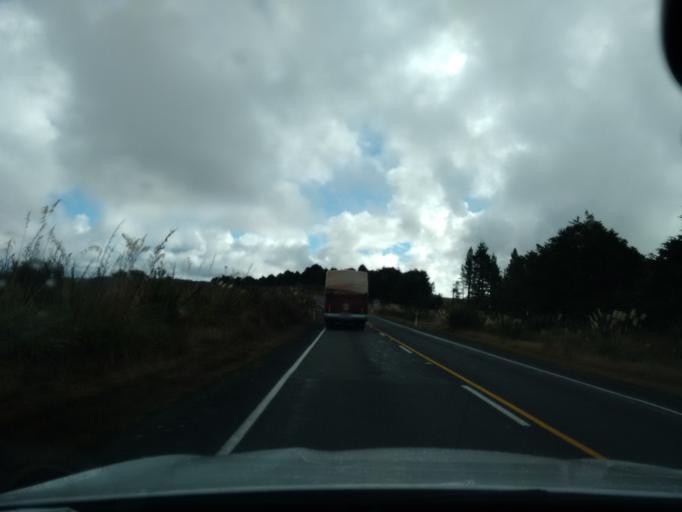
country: NZ
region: Manawatu-Wanganui
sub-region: Ruapehu District
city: Waiouru
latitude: -39.1799
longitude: 175.4507
